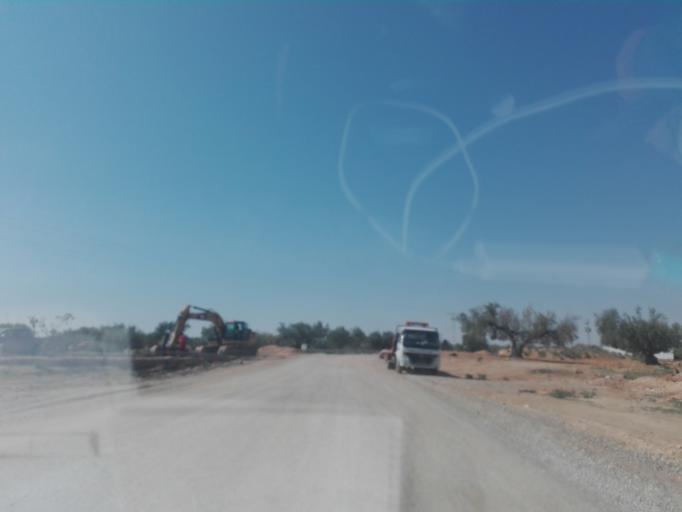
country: TN
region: Safaqis
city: Sfax
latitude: 34.6880
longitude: 10.4644
